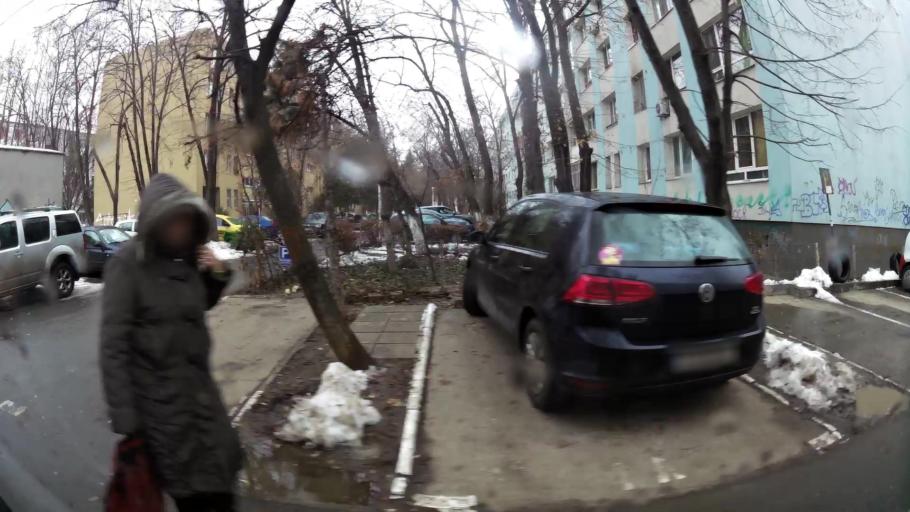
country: RO
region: Ilfov
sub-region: Comuna Chiajna
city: Rosu
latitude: 44.4243
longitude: 26.0193
